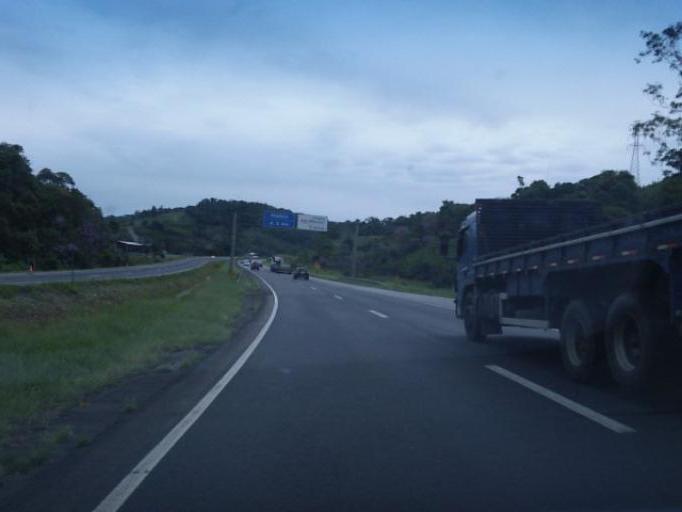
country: BR
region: Sao Paulo
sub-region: Juquia
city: Juquia
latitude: -24.3725
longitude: -47.7066
